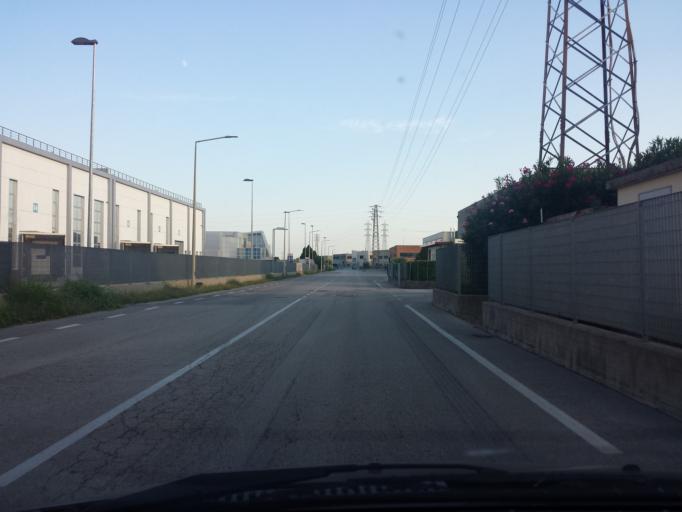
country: IT
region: Veneto
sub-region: Provincia di Vicenza
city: Sandrigo
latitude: 45.6582
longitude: 11.5775
